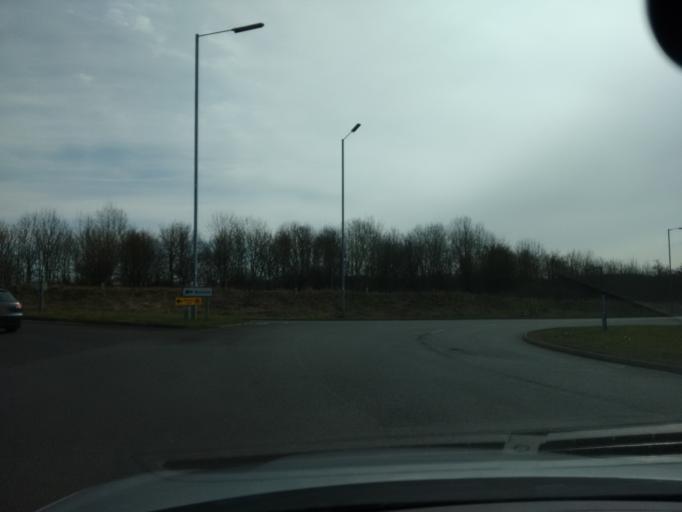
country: GB
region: England
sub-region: Warwickshire
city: Alcester
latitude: 52.2095
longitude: -1.8797
